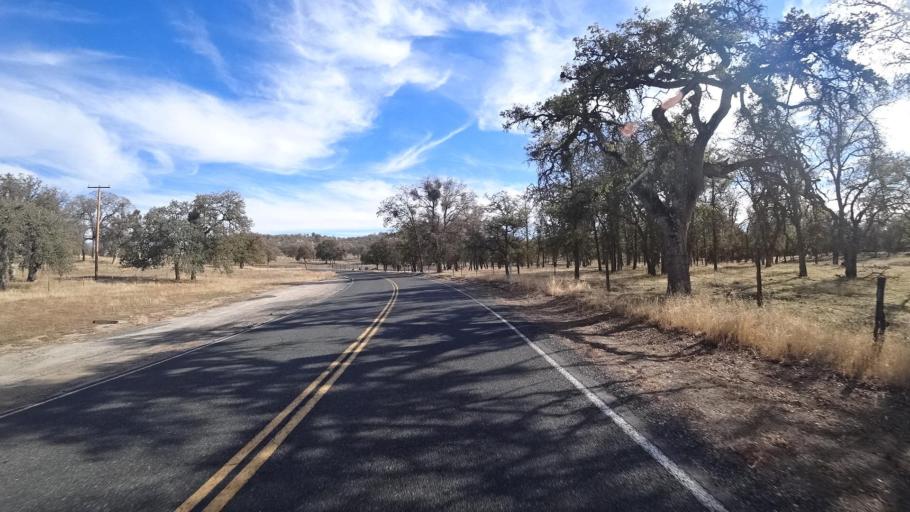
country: US
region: California
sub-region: Kern County
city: Alta Sierra
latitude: 35.6478
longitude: -118.7743
